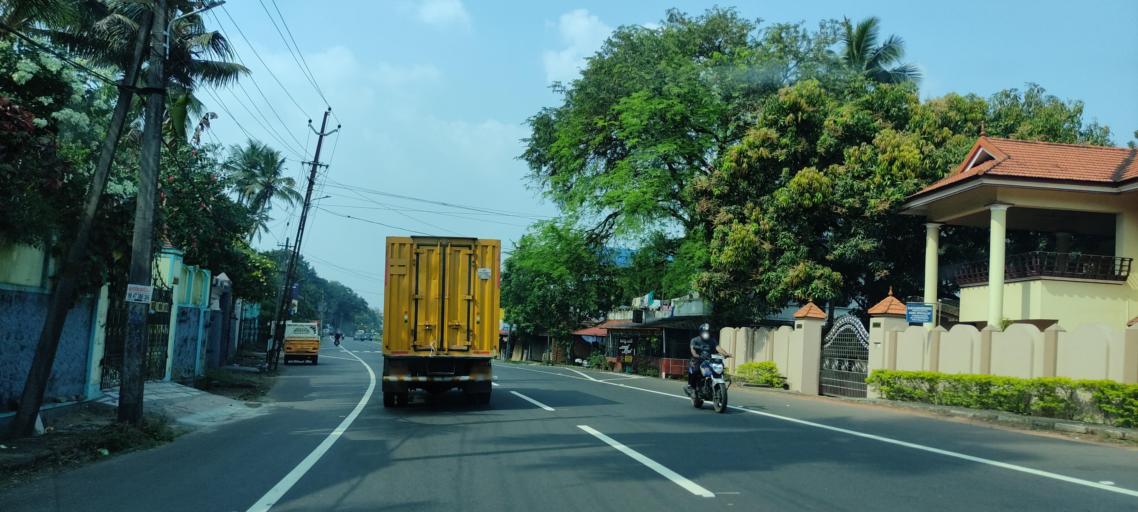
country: IN
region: Kerala
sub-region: Alappuzha
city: Chengannur
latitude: 9.2833
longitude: 76.6543
